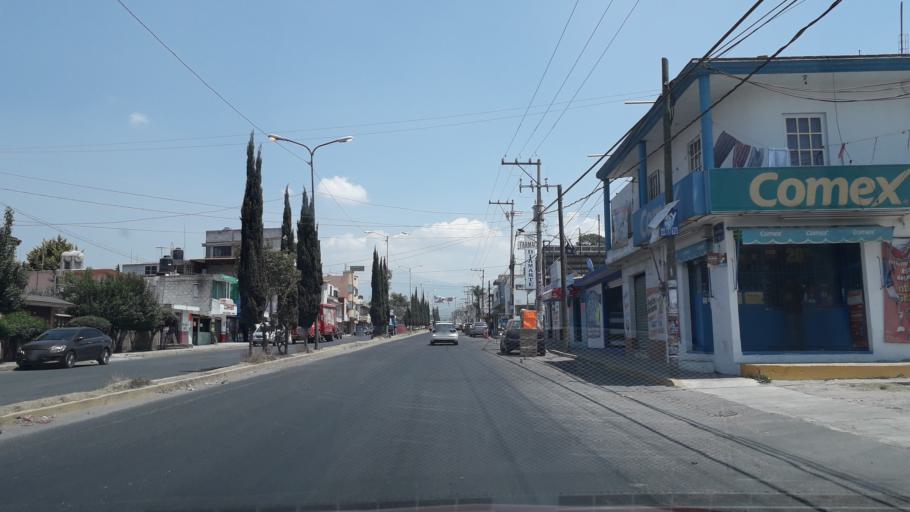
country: MX
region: Puebla
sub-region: Puebla
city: Primero de Mayo
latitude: 19.0696
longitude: -98.1167
